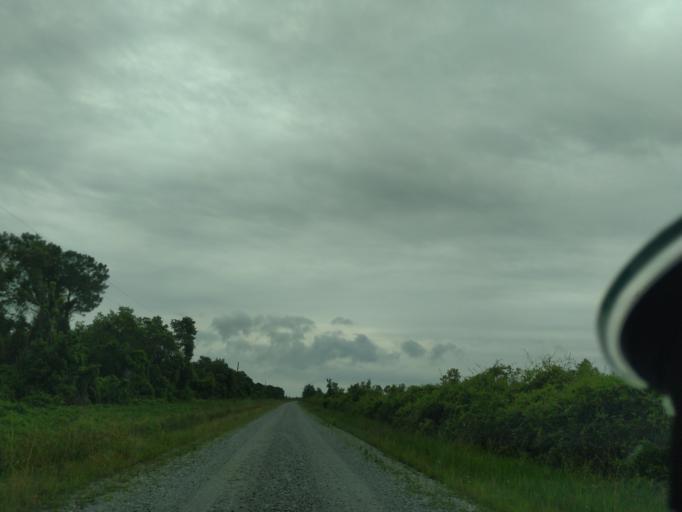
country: US
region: North Carolina
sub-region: Beaufort County
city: Belhaven
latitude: 35.7400
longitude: -76.4750
